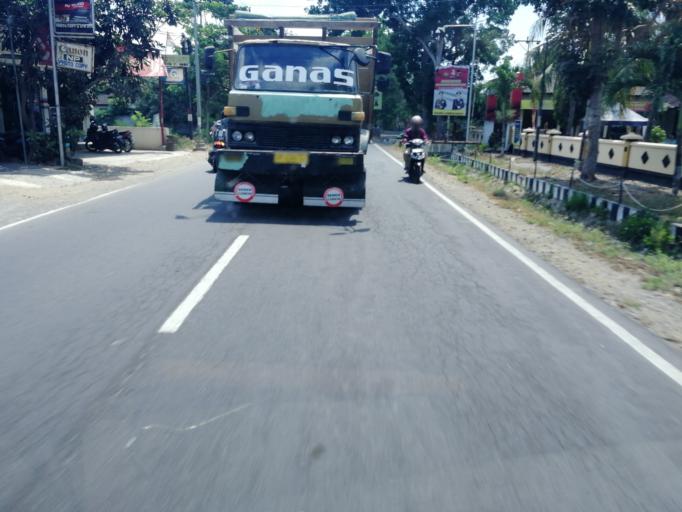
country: ID
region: West Nusa Tenggara
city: Jelateng Timur
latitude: -8.7046
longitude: 116.0892
